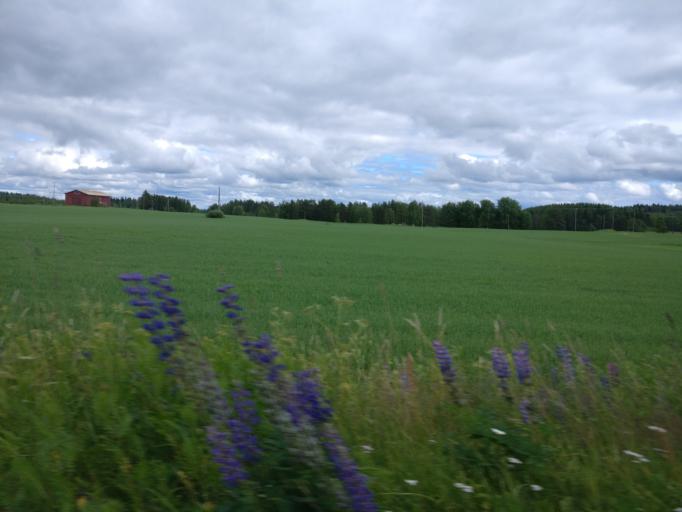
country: FI
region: Northern Savo
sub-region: Koillis-Savo
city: Juankoski
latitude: 63.0079
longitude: 28.2398
